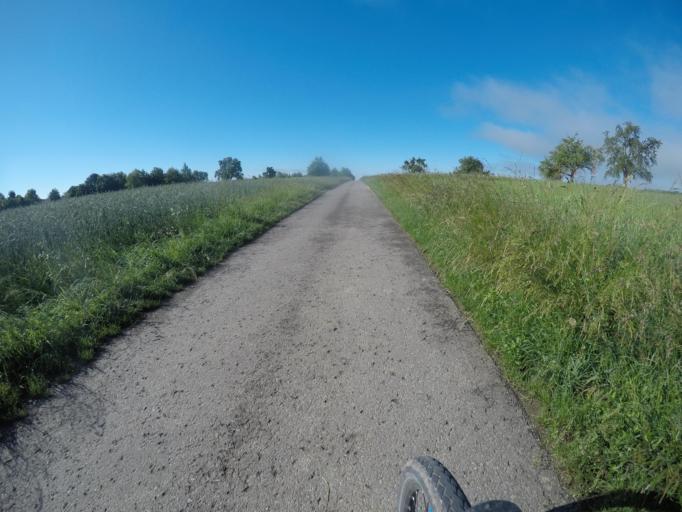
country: DE
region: Baden-Wuerttemberg
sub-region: Regierungsbezirk Stuttgart
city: Nufringen
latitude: 48.6378
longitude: 8.8806
